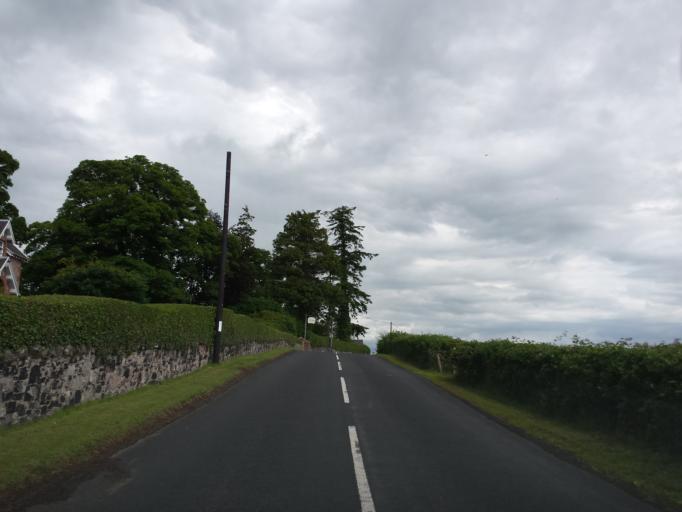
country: GB
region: Scotland
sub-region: The Scottish Borders
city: Saint Boswells
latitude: 55.5858
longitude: -2.6301
